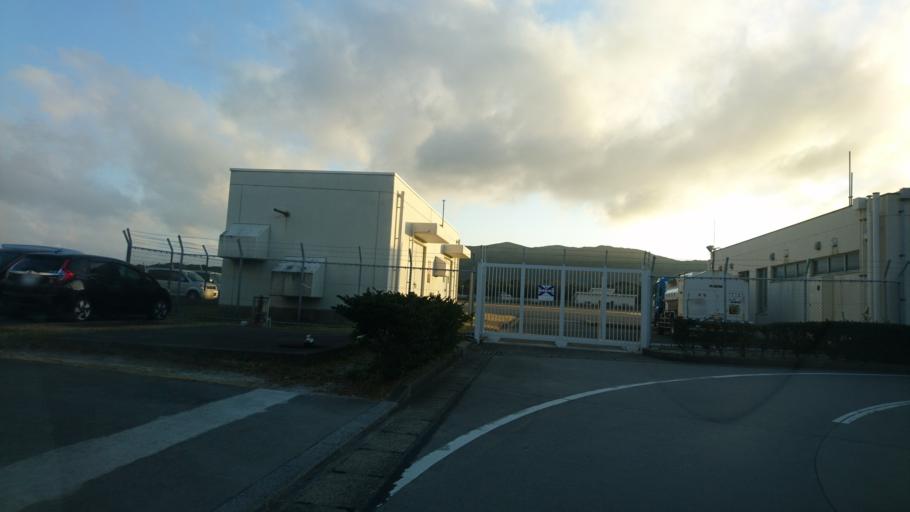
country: JP
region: Shizuoka
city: Shimoda
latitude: 34.3706
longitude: 139.2697
